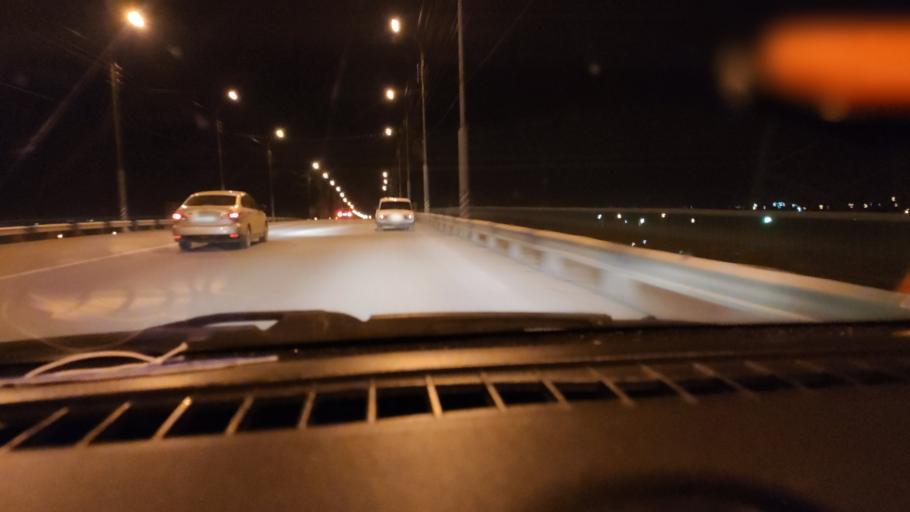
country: RU
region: Saratov
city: Privolzhskiy
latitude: 51.4162
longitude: 46.0451
